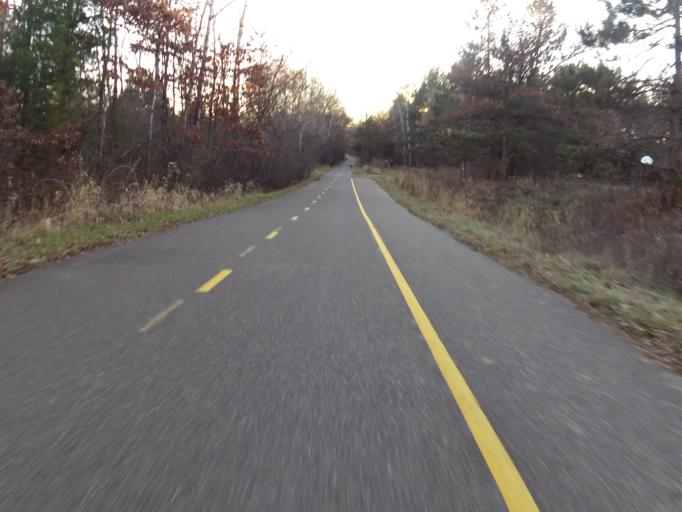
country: US
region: Minnesota
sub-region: Washington County
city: Grant
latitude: 45.1037
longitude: -92.8661
